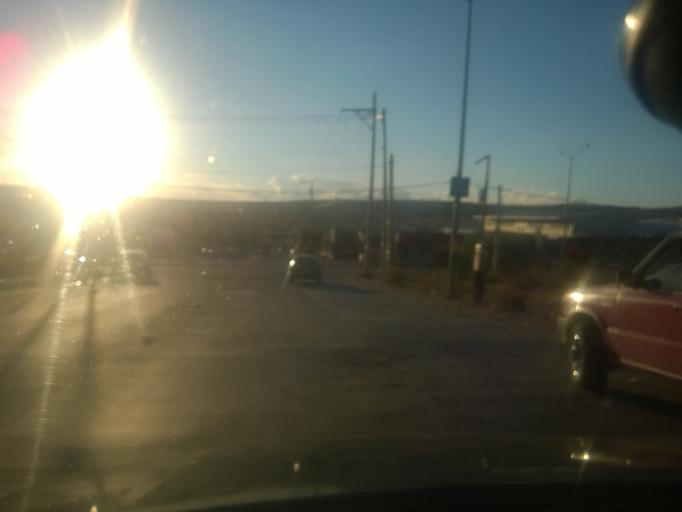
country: MX
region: Guanajuato
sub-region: Leon
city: La Ermita
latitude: 21.1533
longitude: -101.7363
